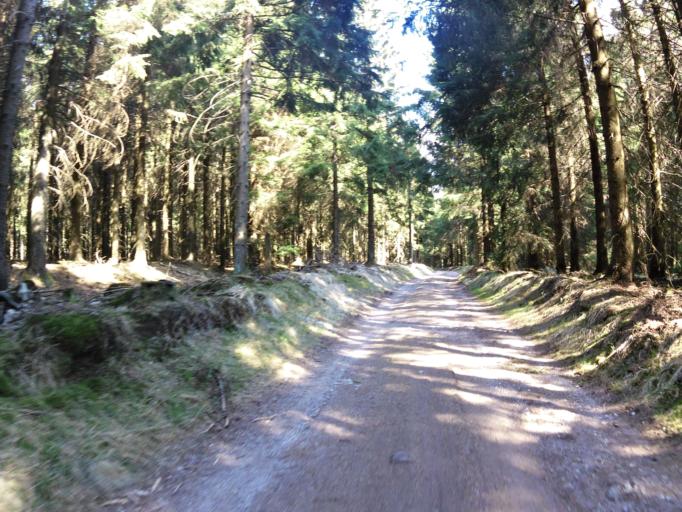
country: DE
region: Thuringia
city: Unterschonau
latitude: 50.7381
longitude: 10.6095
